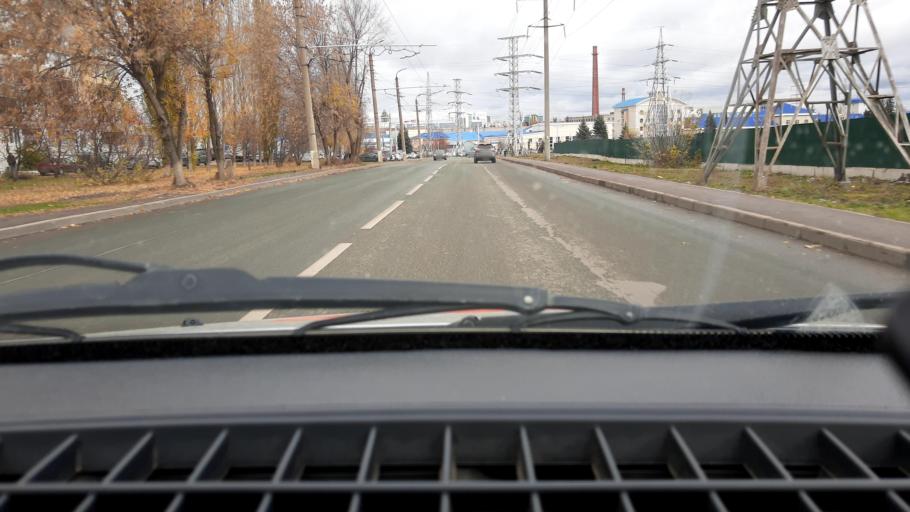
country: RU
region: Bashkortostan
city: Ufa
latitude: 54.7954
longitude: 56.0564
